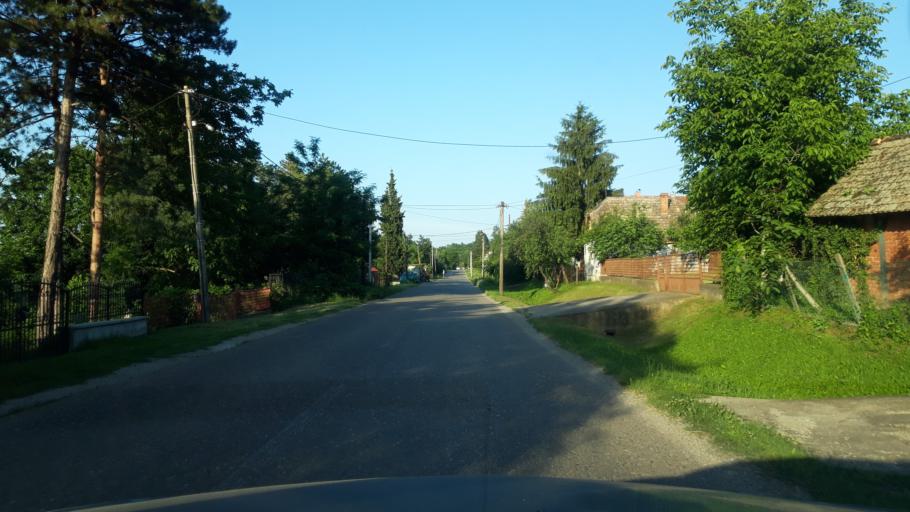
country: RS
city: Glozan
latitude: 45.2153
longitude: 19.6203
